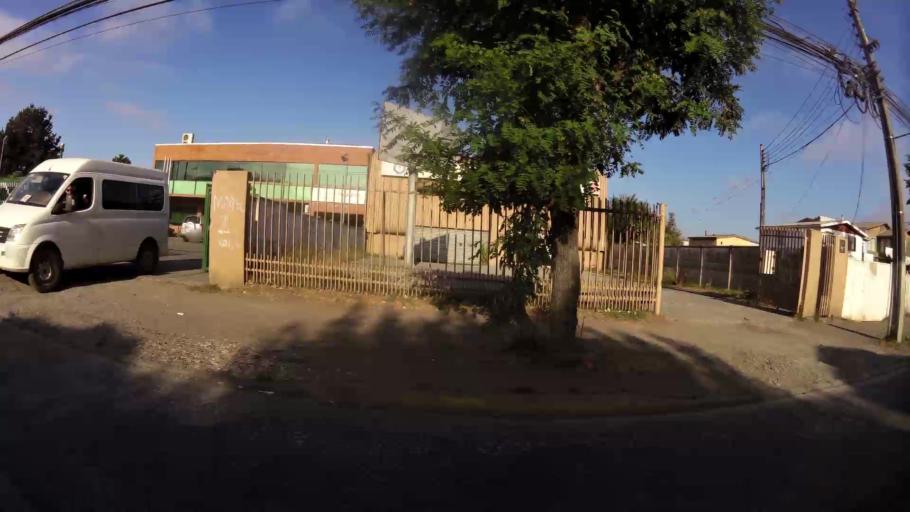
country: CL
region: Biobio
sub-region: Provincia de Concepcion
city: Concepcion
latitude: -36.7877
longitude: -73.0868
